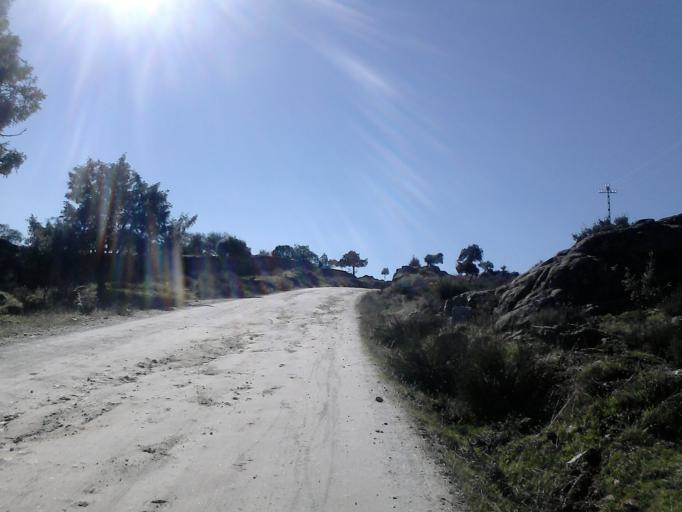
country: ES
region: Madrid
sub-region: Provincia de Madrid
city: Galapagar
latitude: 40.5575
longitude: -3.9824
